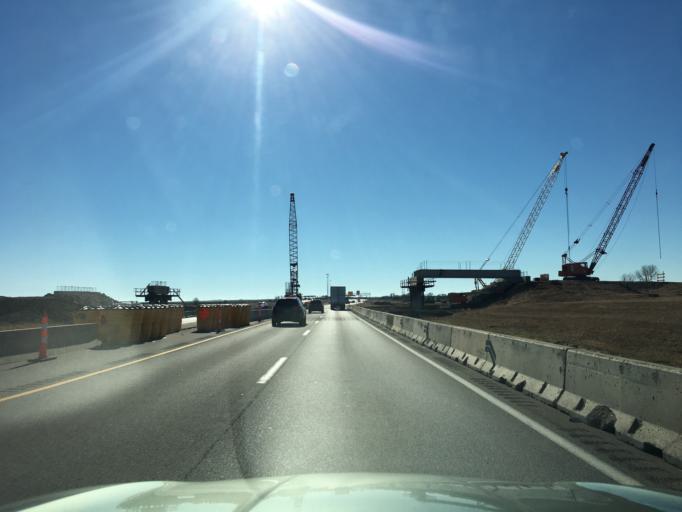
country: US
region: Kansas
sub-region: Sumner County
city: Wellington
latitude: 37.2480
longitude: -97.3390
